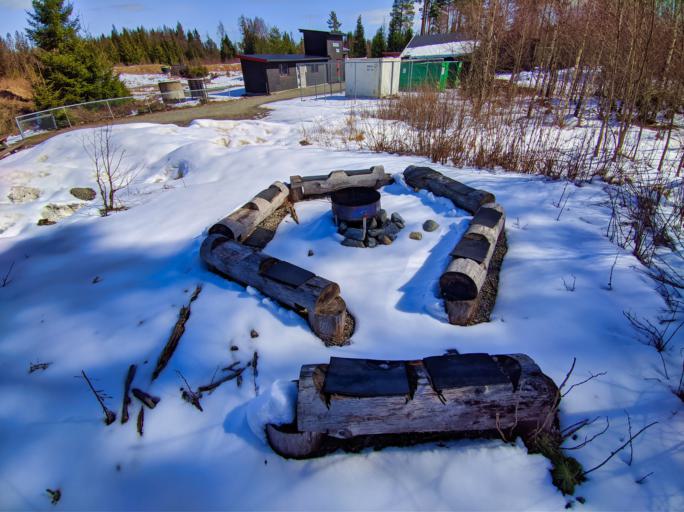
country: NO
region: Akershus
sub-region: Ullensaker
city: Jessheim
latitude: 60.1845
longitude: 11.1294
